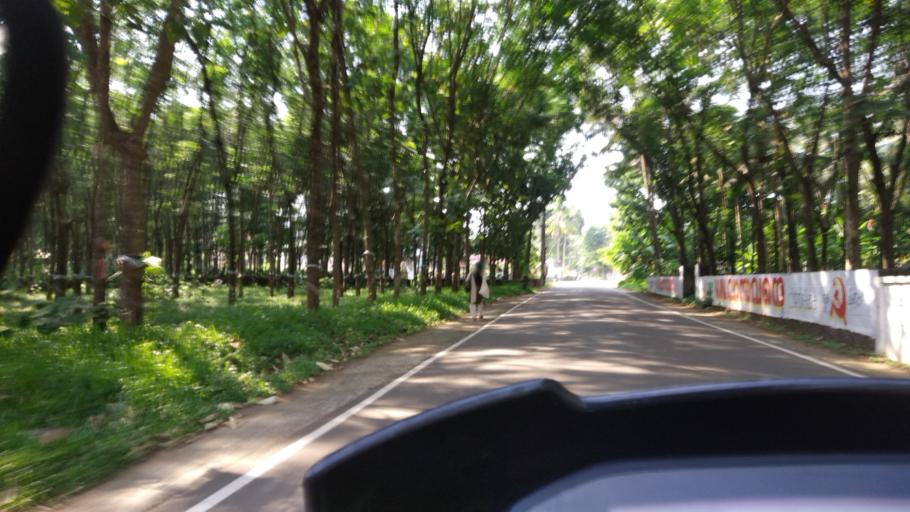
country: IN
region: Kerala
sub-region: Ernakulam
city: Piravam
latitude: 9.8337
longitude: 76.5420
